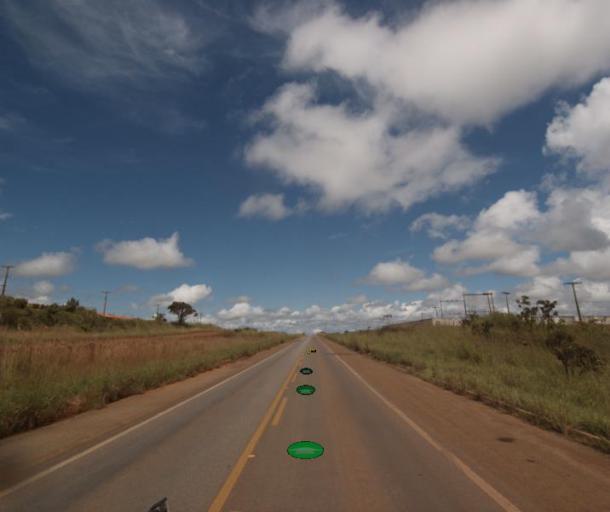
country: BR
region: Federal District
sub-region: Brasilia
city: Brasilia
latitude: -15.7428
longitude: -48.4103
